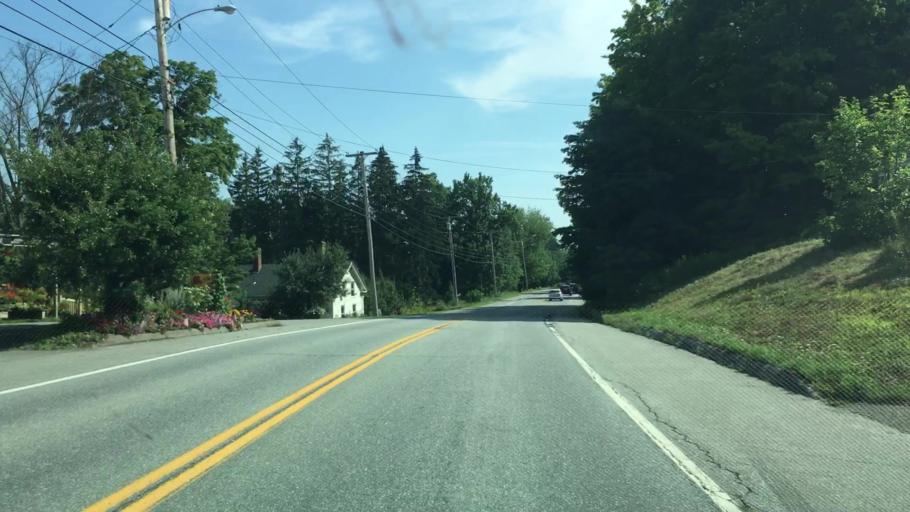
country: US
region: Maine
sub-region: Penobscot County
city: Orrington
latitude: 44.7202
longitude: -68.8451
